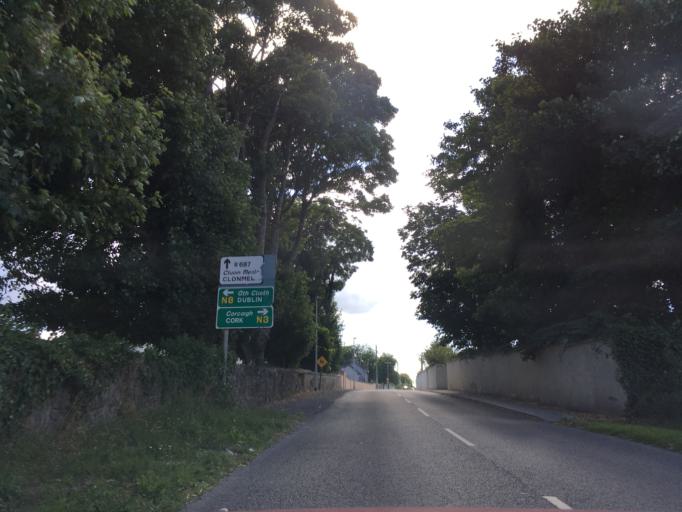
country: IE
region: Munster
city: Cashel
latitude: 52.4420
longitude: -7.8859
